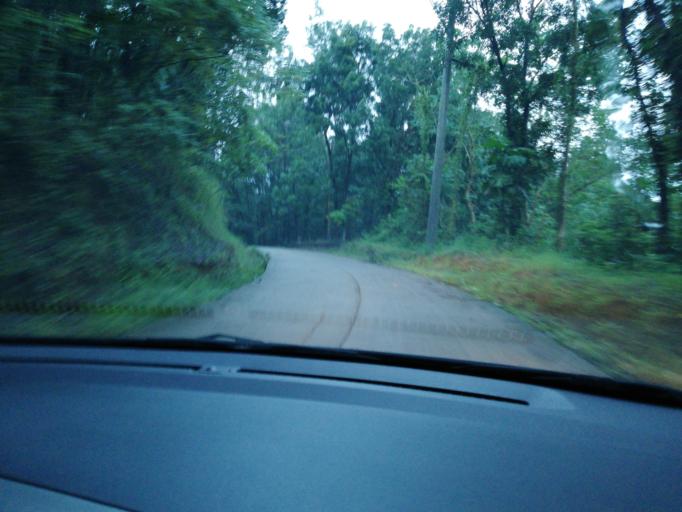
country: PH
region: Calabarzon
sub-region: Province of Rizal
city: Rodriguez
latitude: 14.7841
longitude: 121.1369
